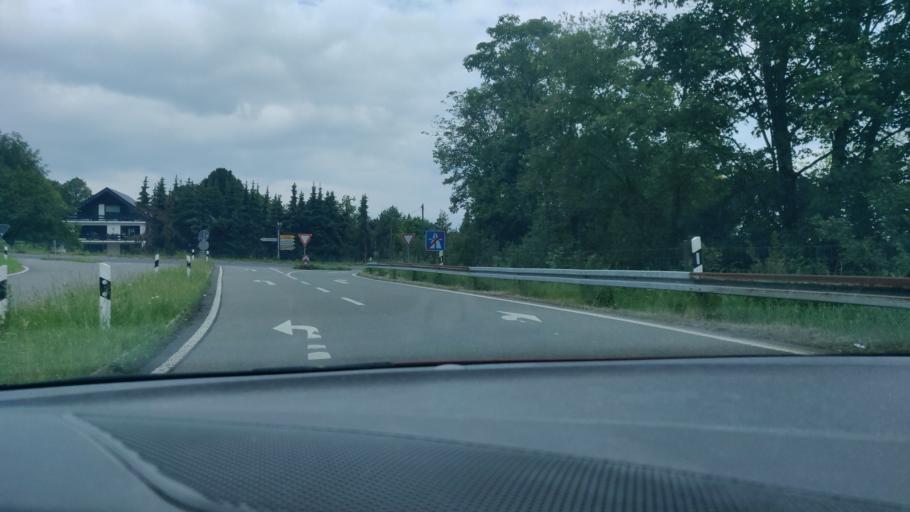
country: DE
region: North Rhine-Westphalia
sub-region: Regierungsbezirk Dusseldorf
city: Velbert
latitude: 51.3182
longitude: 7.0727
